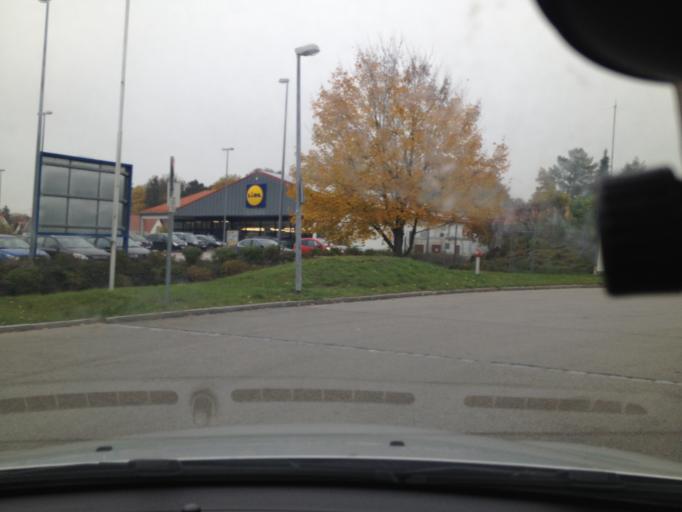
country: DE
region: Bavaria
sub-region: Swabia
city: Schwabmunchen
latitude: 48.1697
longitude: 10.7564
